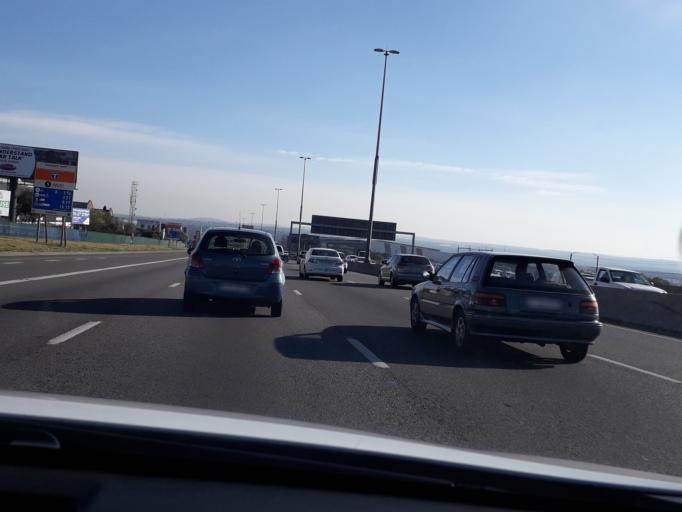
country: ZA
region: Gauteng
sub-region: City of Tshwane Metropolitan Municipality
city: Centurion
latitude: -25.9010
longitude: 28.1620
